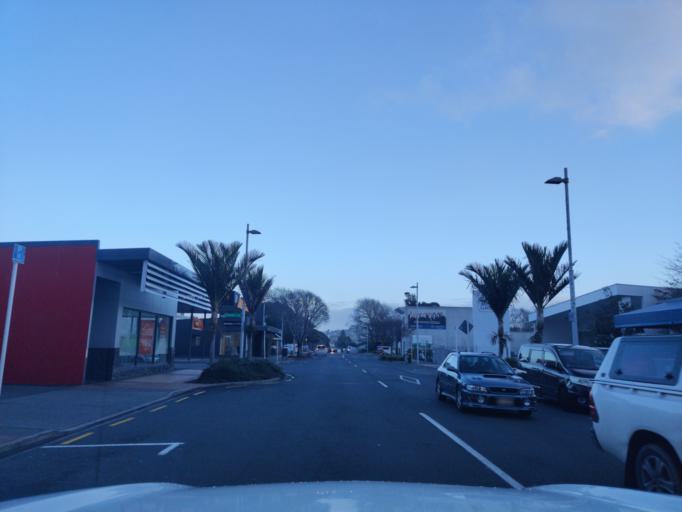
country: NZ
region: Auckland
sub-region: Auckland
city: Pukekohe East
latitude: -37.2008
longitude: 174.9012
